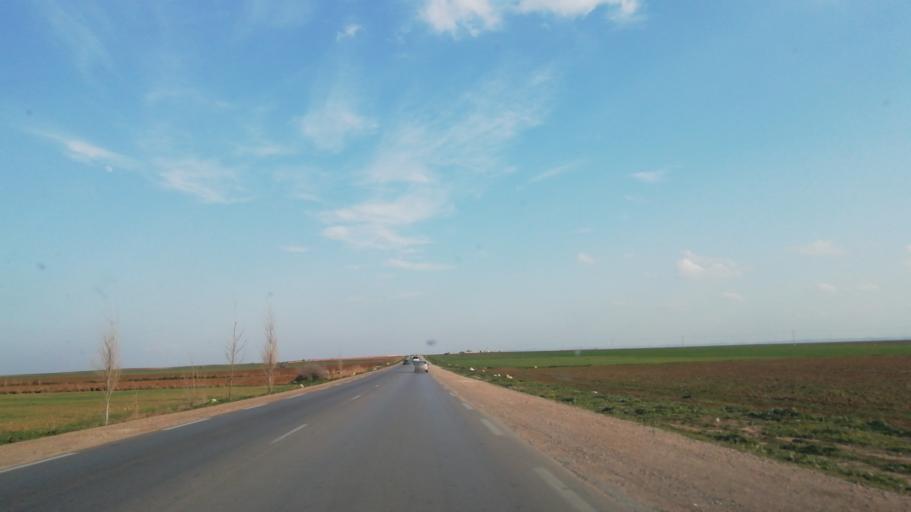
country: DZ
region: Relizane
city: Relizane
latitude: 35.8957
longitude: 0.5999
